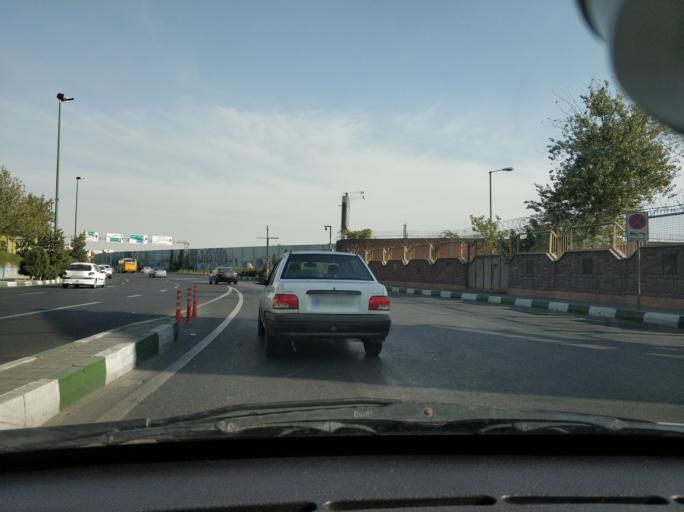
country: IR
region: Tehran
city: Tehran
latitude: 35.6981
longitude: 51.3353
